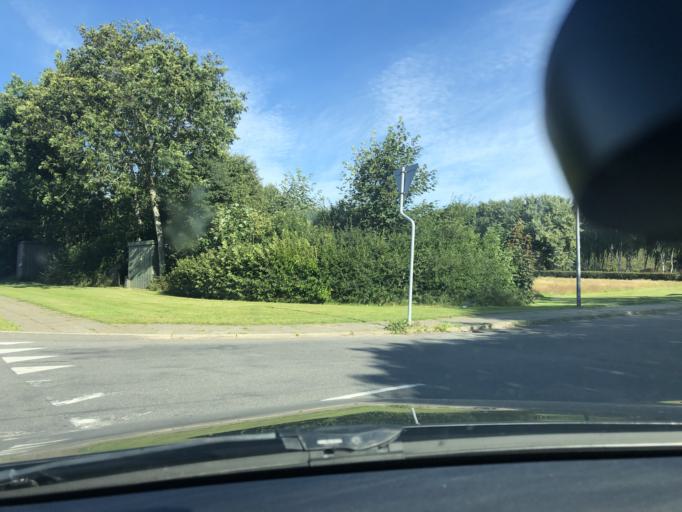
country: DK
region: South Denmark
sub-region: Varde Kommune
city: Olgod
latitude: 55.8081
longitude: 8.6074
